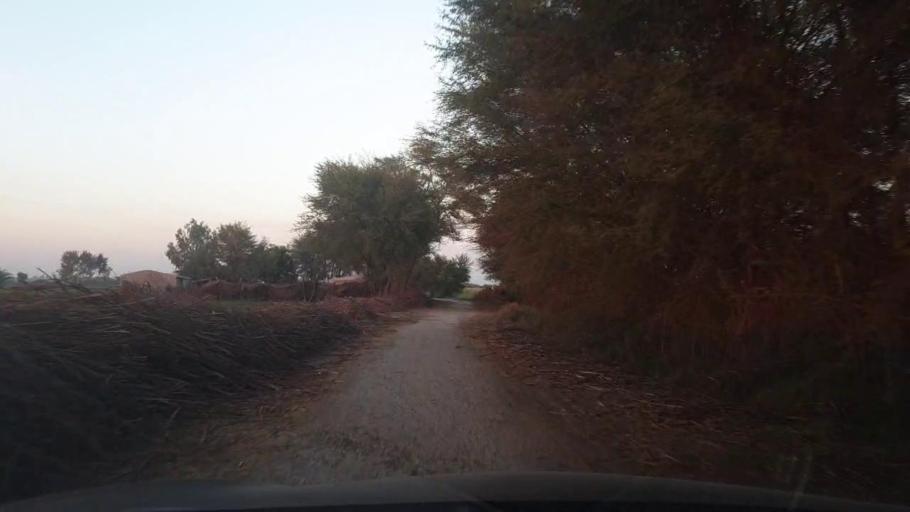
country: PK
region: Sindh
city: Ubauro
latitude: 28.1707
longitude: 69.6353
